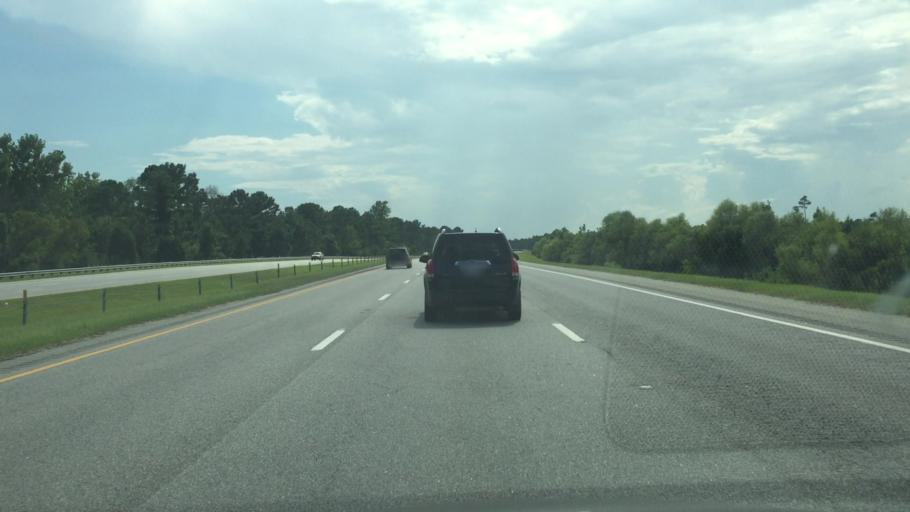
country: US
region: South Carolina
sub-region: Horry County
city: Myrtle Beach
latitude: 33.7723
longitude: -78.8213
